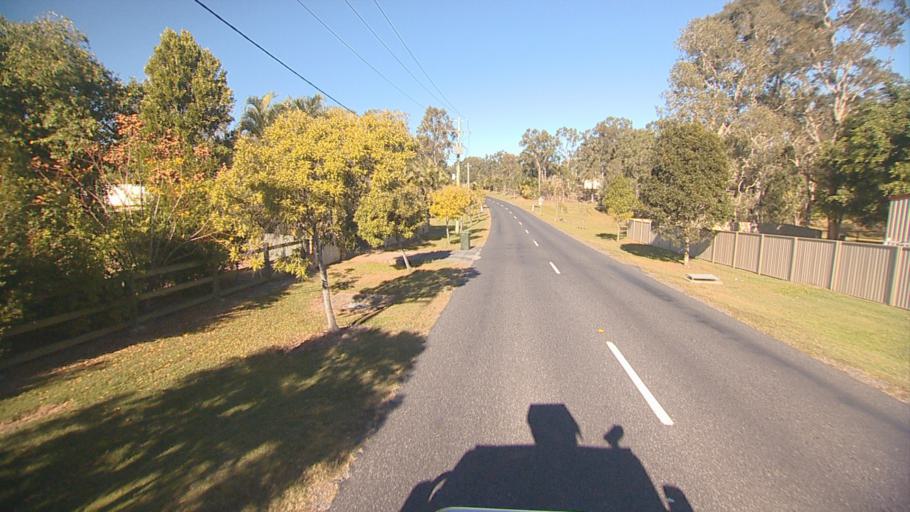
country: AU
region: Queensland
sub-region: Logan
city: North Maclean
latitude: -27.7402
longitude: 152.9689
